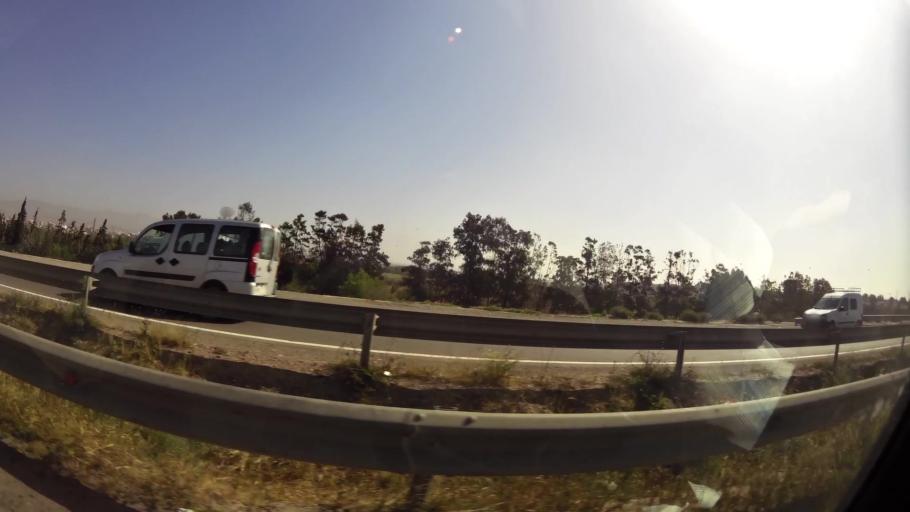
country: MA
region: Souss-Massa-Draa
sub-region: Inezgane-Ait Mellou
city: Inezgane
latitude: 30.3614
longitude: -9.4917
